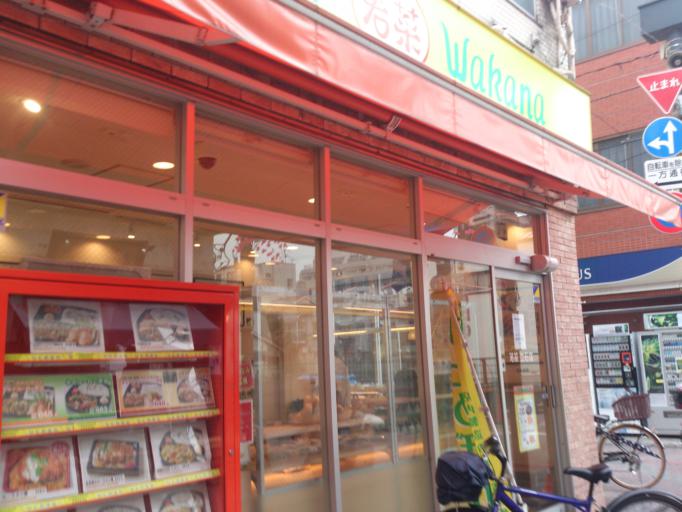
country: JP
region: Chiba
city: Matsudo
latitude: 35.7392
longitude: 139.8491
